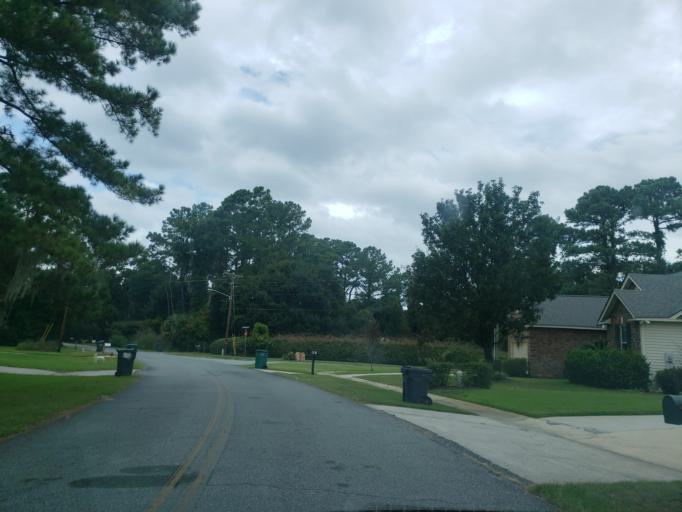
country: US
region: Georgia
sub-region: Chatham County
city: Wilmington Island
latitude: 32.0147
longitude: -80.9545
